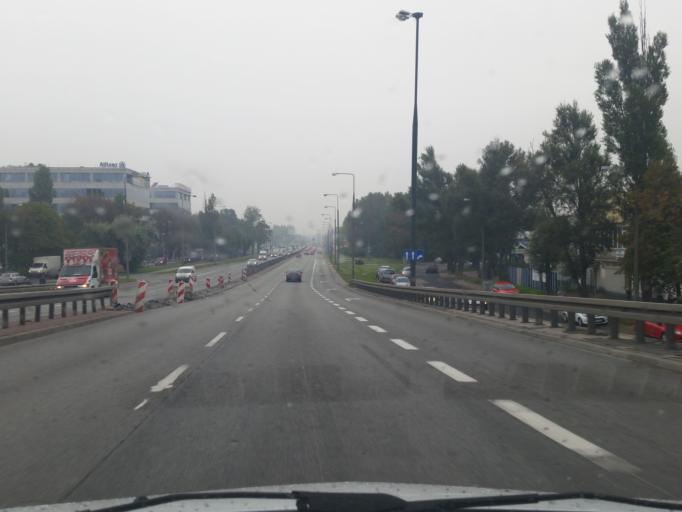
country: PL
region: Masovian Voivodeship
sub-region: Warszawa
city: Wlochy
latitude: 52.1941
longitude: 20.9377
